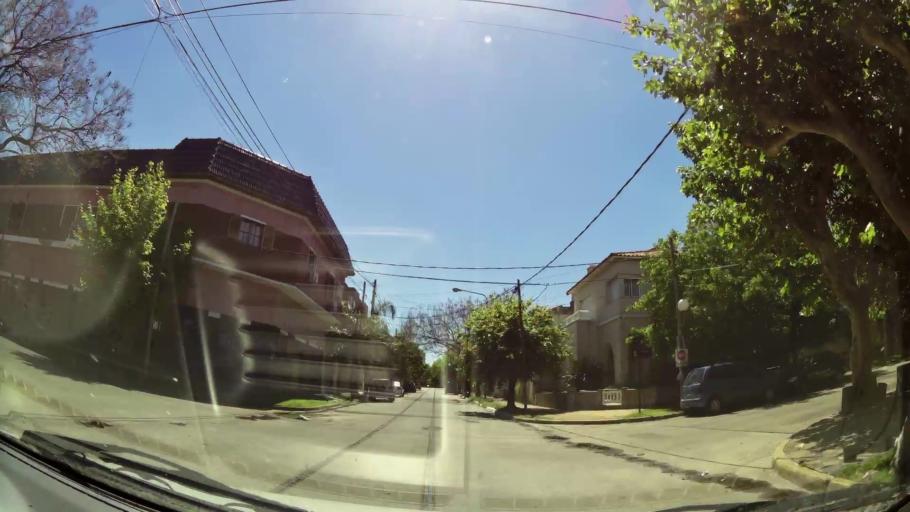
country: AR
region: Buenos Aires
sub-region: Partido de Quilmes
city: Quilmes
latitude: -34.7167
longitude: -58.2898
